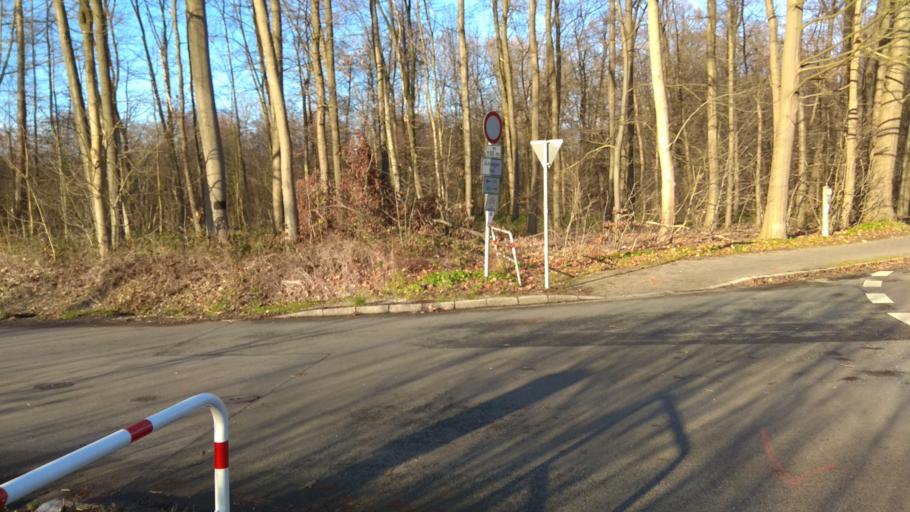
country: DE
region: North Rhine-Westphalia
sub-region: Regierungsbezirk Munster
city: Recklinghausen
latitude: 51.5924
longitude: 7.1971
